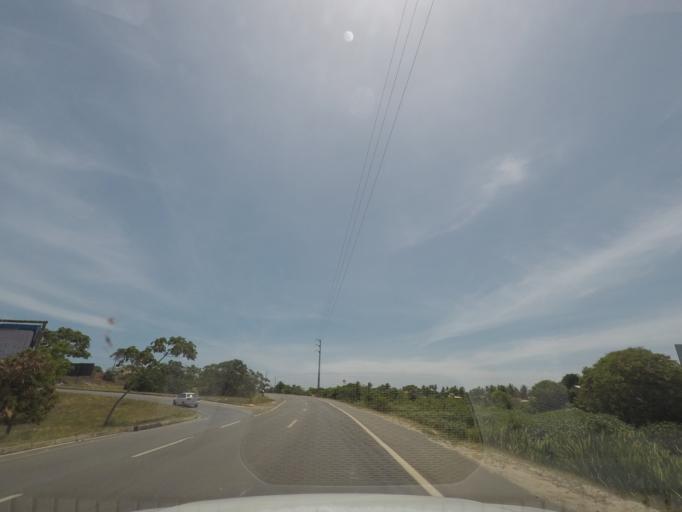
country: BR
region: Bahia
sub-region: Camacari
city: Camacari
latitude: -12.6547
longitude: -38.0868
